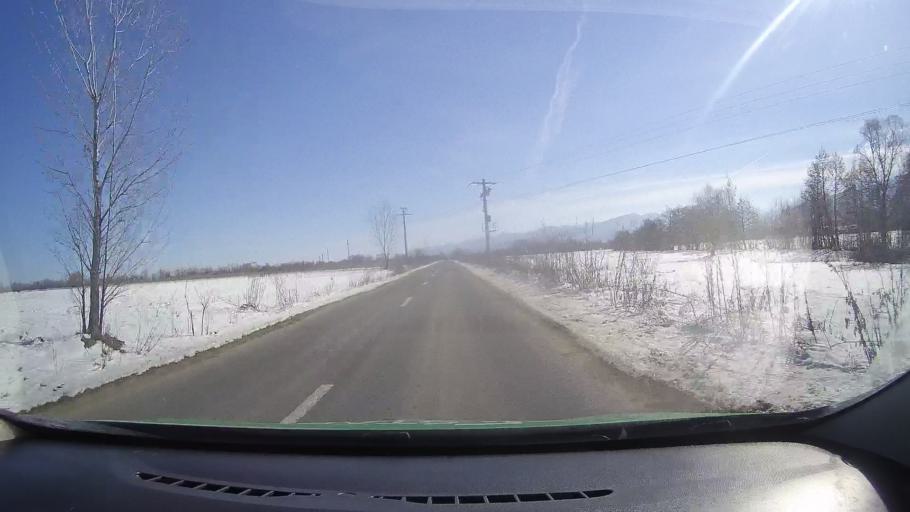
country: RO
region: Brasov
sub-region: Comuna Harseni
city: Harseni
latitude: 45.7339
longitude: 25.0143
